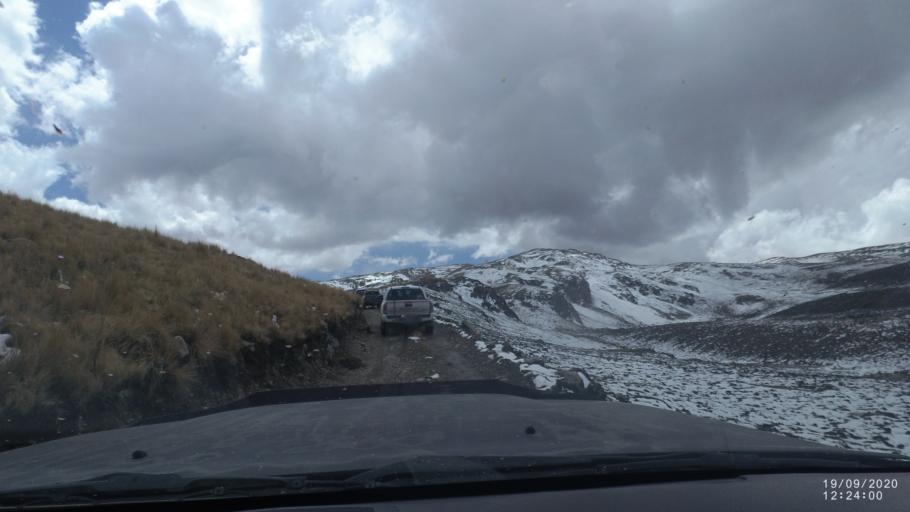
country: BO
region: Cochabamba
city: Cochabamba
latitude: -17.2947
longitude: -66.1104
